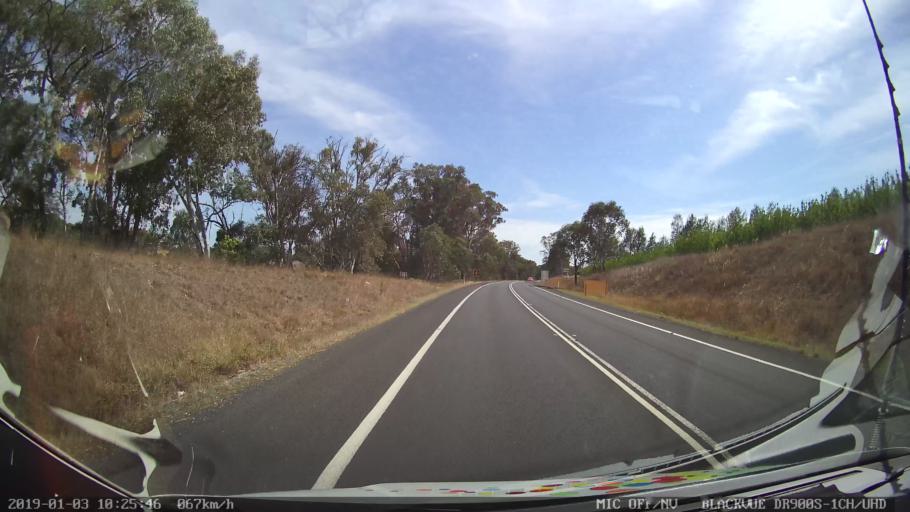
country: AU
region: New South Wales
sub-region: Young
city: Young
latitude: -34.4197
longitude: 148.2445
